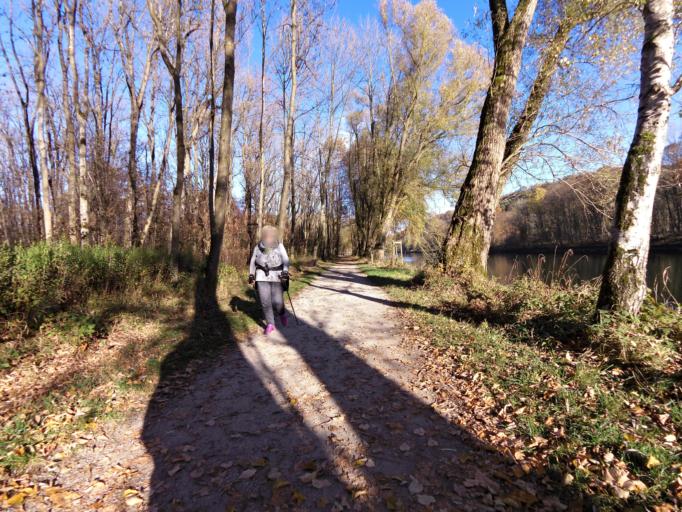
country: DE
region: Bavaria
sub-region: Lower Bavaria
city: Tiefenbach
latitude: 48.5245
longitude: 12.1224
